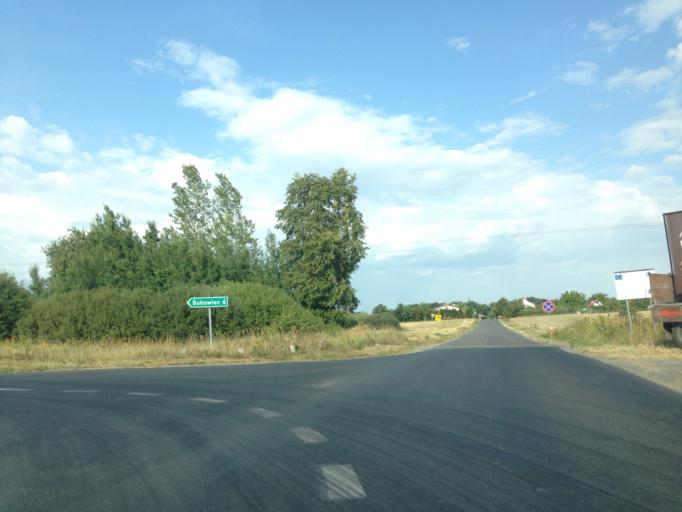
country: PL
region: Kujawsko-Pomorskie
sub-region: Powiat swiecki
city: Bukowiec
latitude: 53.3900
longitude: 18.2947
